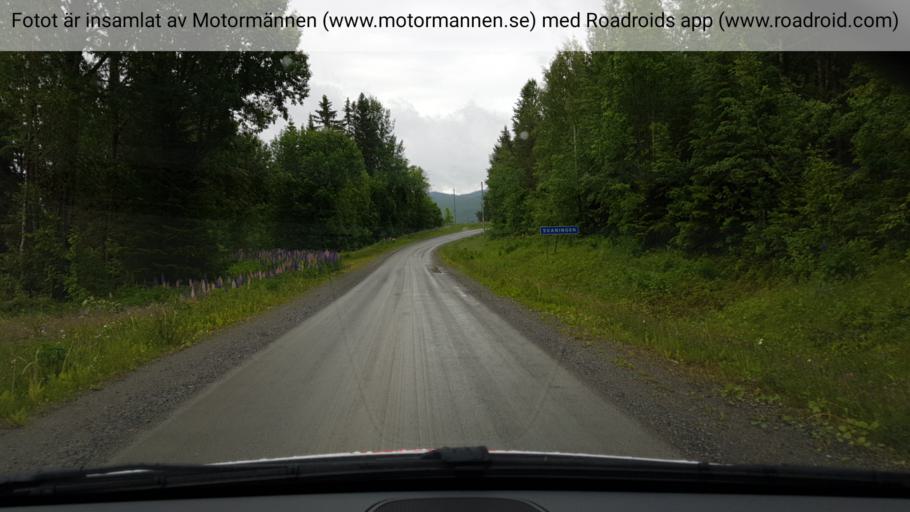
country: SE
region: Jaemtland
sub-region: Stroemsunds Kommun
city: Stroemsund
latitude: 64.2851
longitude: 15.0153
